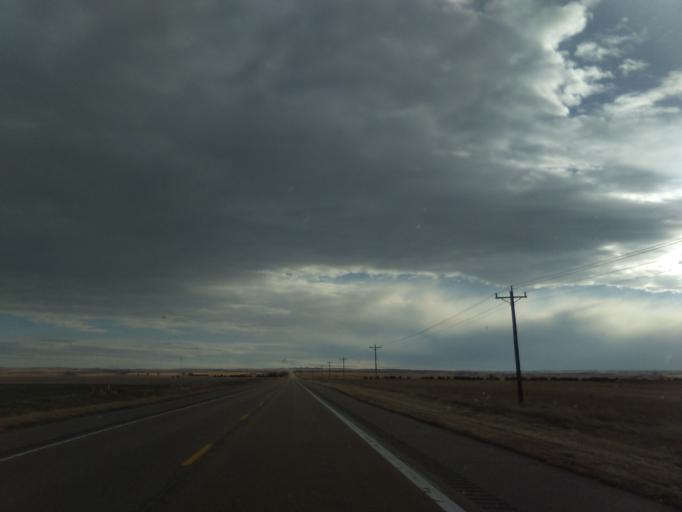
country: US
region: Nebraska
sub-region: Morrill County
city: Bridgeport
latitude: 41.5528
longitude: -102.9845
